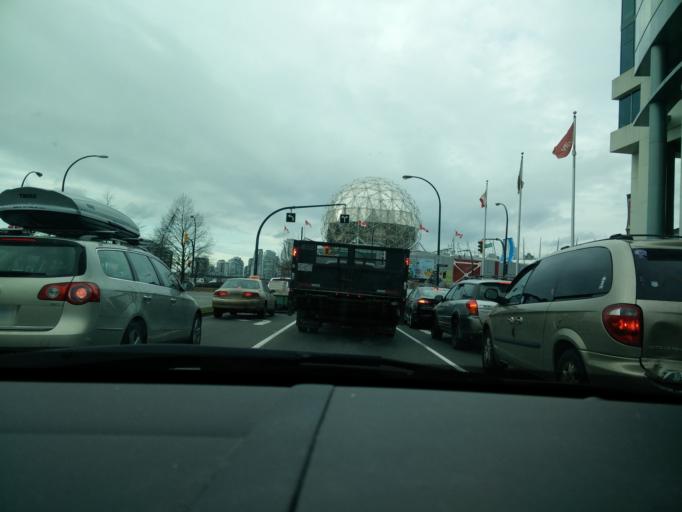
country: CA
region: British Columbia
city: Vancouver
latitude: 49.2731
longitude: -123.1009
